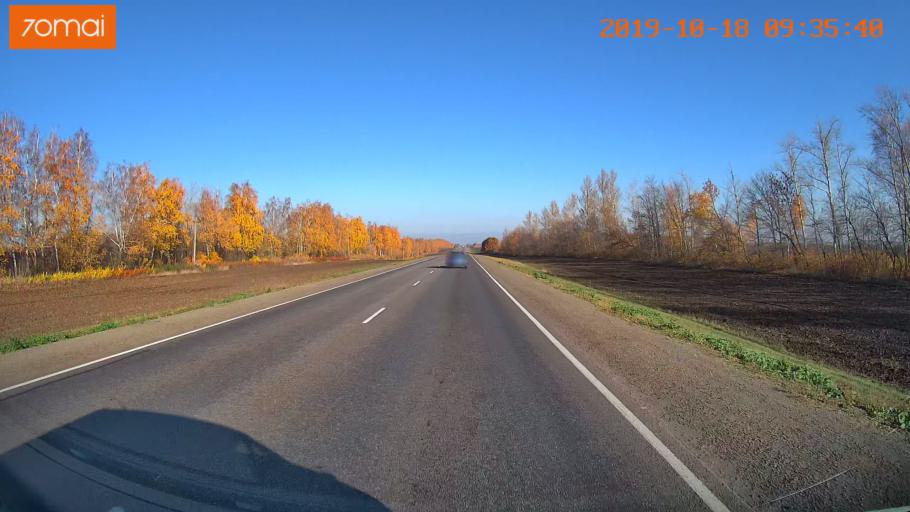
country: RU
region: Tula
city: Yefremov
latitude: 53.1953
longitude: 38.1478
